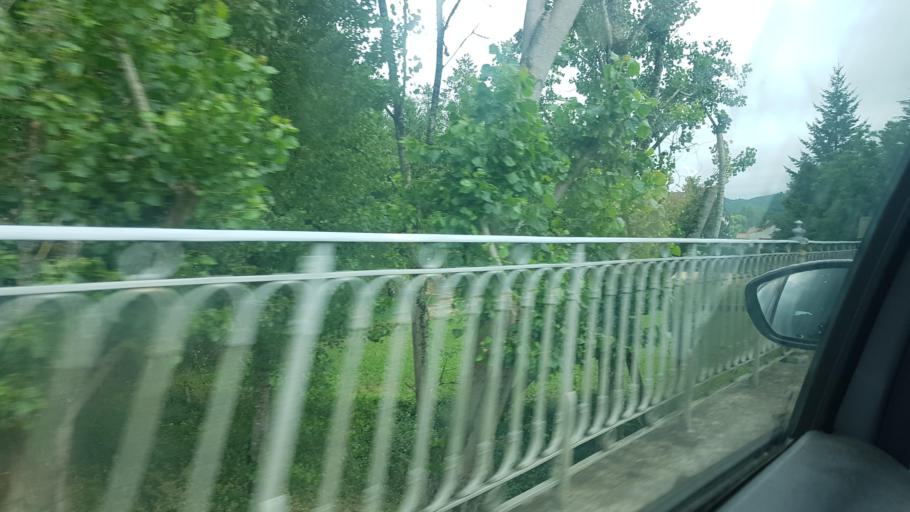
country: FR
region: Aquitaine
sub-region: Departement du Lot-et-Garonne
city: Montayral
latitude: 44.4939
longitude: 1.0827
